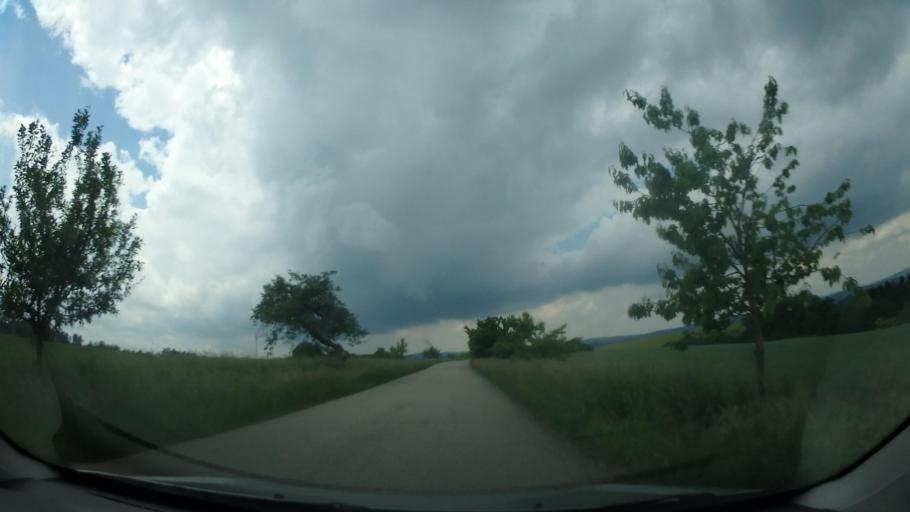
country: CZ
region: South Moravian
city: Boritov
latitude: 49.4553
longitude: 16.5998
